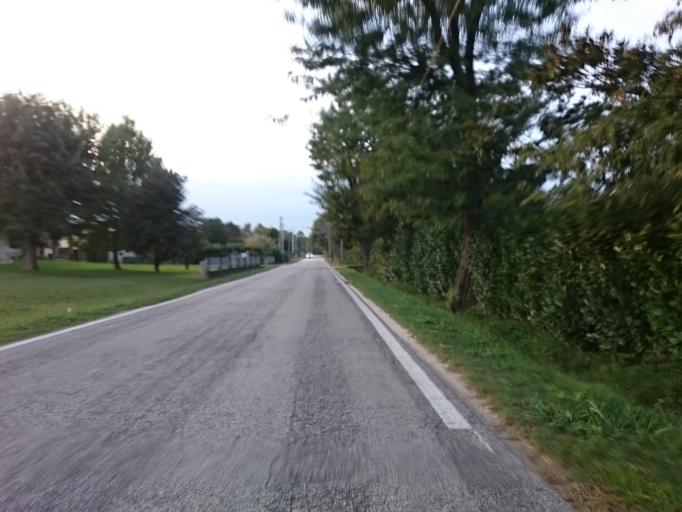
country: IT
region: Veneto
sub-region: Provincia di Vicenza
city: Grisignano di Zocco
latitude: 45.4872
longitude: 11.7217
